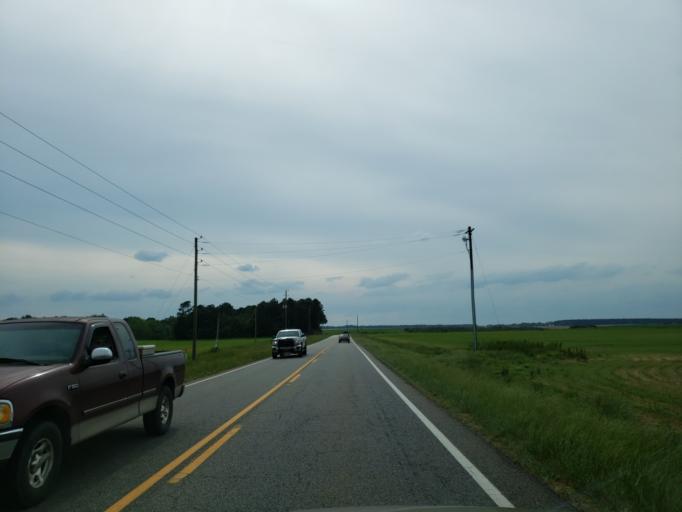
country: US
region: Georgia
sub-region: Macon County
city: Marshallville
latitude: 32.3664
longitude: -83.9112
